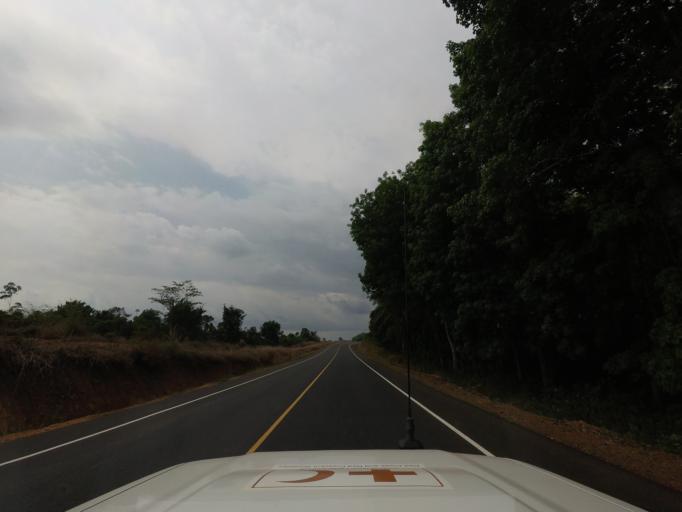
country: LR
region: Margibi
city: Kakata
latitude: 6.4967
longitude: -10.3913
